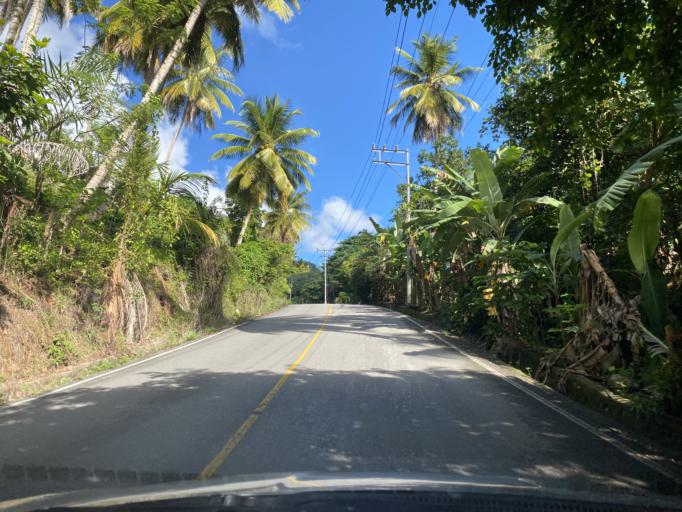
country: DO
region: Samana
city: Sanchez
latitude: 19.2337
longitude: -69.6008
